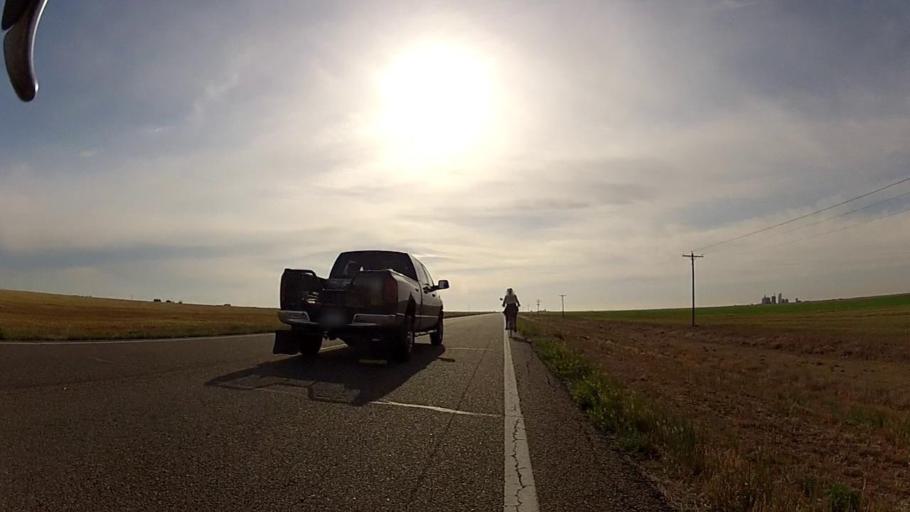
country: US
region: Kansas
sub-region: Grant County
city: Ulysses
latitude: 37.5766
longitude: -101.4794
